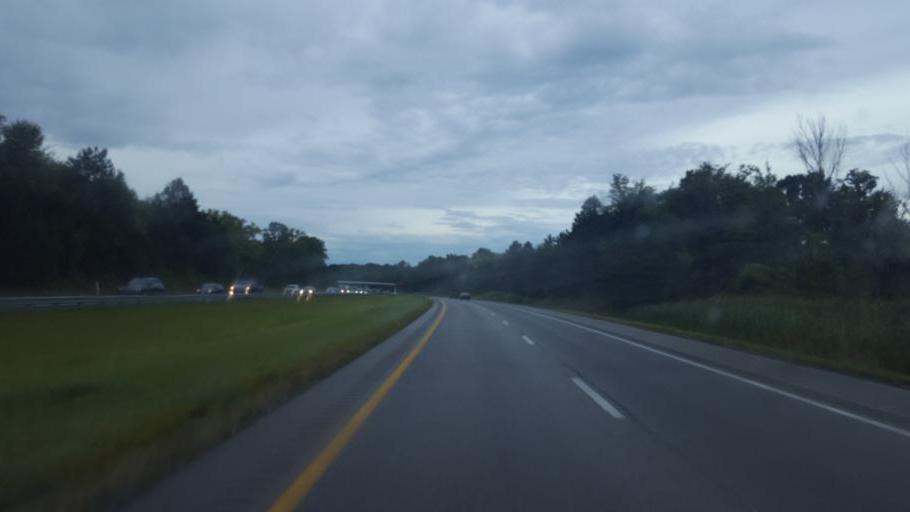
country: US
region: Ohio
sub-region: Cuyahoga County
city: Orange
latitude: 41.4198
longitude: -81.4773
